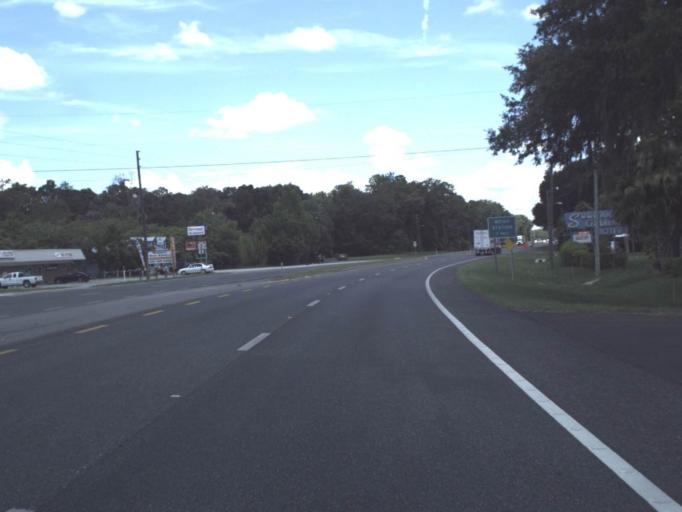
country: US
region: Florida
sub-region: Levy County
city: Manatee Road
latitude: 29.5849
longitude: -82.9567
